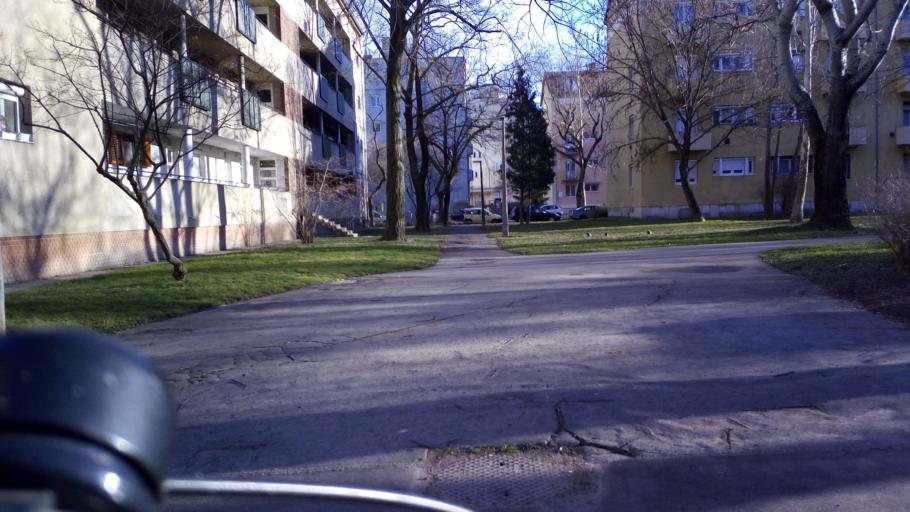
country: HU
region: Baranya
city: Pecs
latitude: 46.0662
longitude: 18.1980
